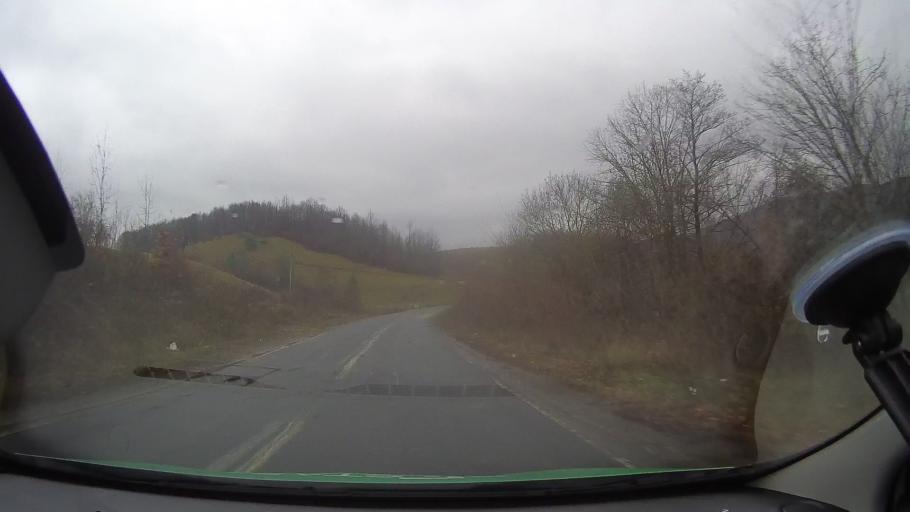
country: RO
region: Arad
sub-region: Comuna Halmagiu
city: Halmagiu
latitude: 46.2429
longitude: 22.5633
